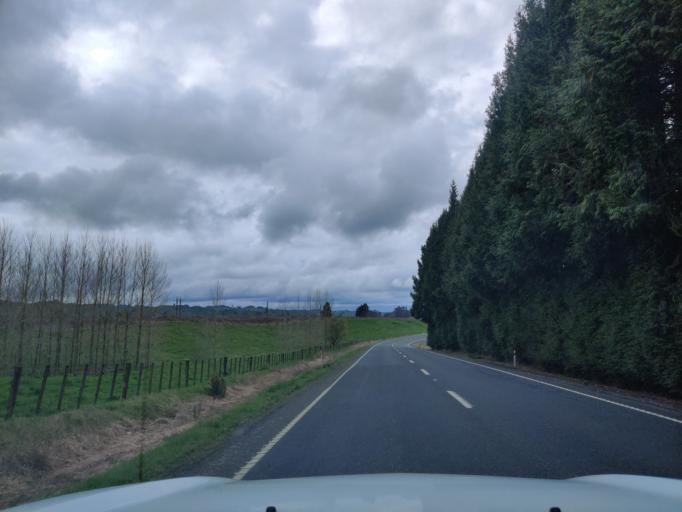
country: NZ
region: Waikato
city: Turangi
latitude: -39.0337
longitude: 175.3821
